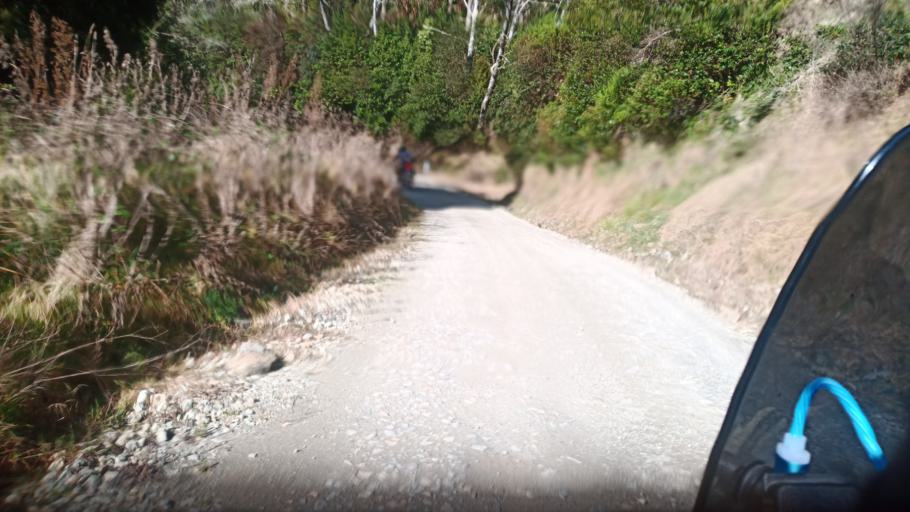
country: NZ
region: Hawke's Bay
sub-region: Wairoa District
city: Wairoa
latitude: -38.6637
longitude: 177.5089
